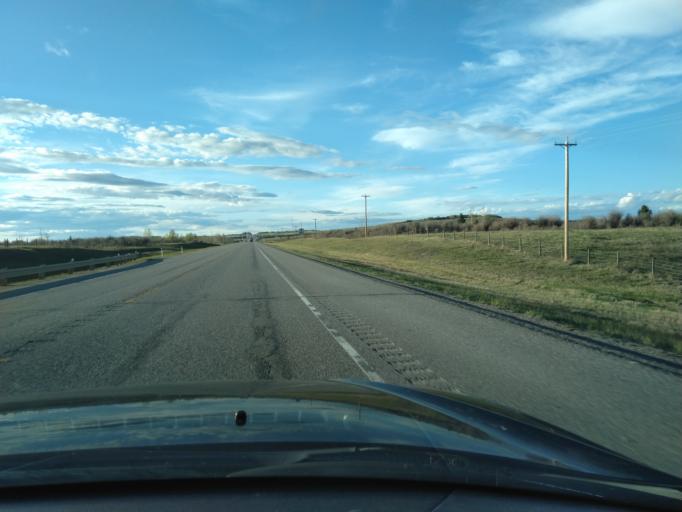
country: CA
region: Alberta
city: Cochrane
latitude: 51.0705
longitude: -114.4668
